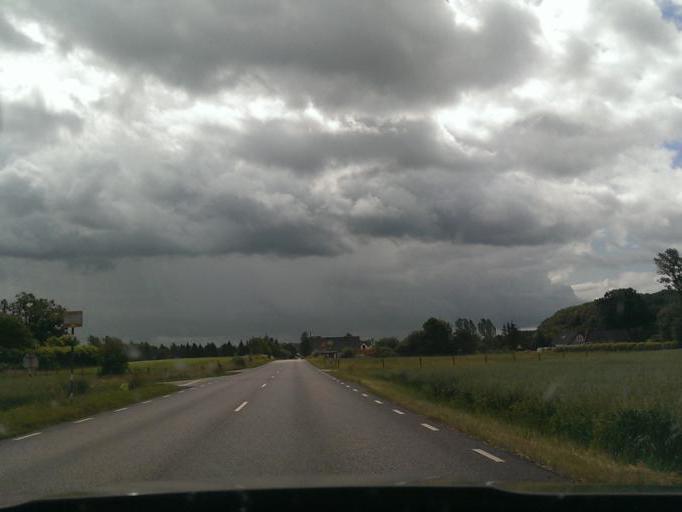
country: SE
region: Skane
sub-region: Eslovs Kommun
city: Stehag
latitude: 55.9792
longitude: 13.3251
